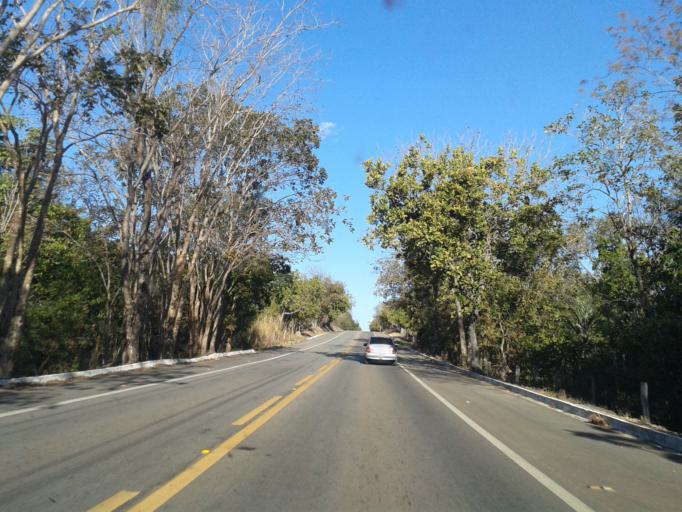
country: BR
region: Goias
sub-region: Itapuranga
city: Itapuranga
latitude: -15.4754
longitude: -50.3396
